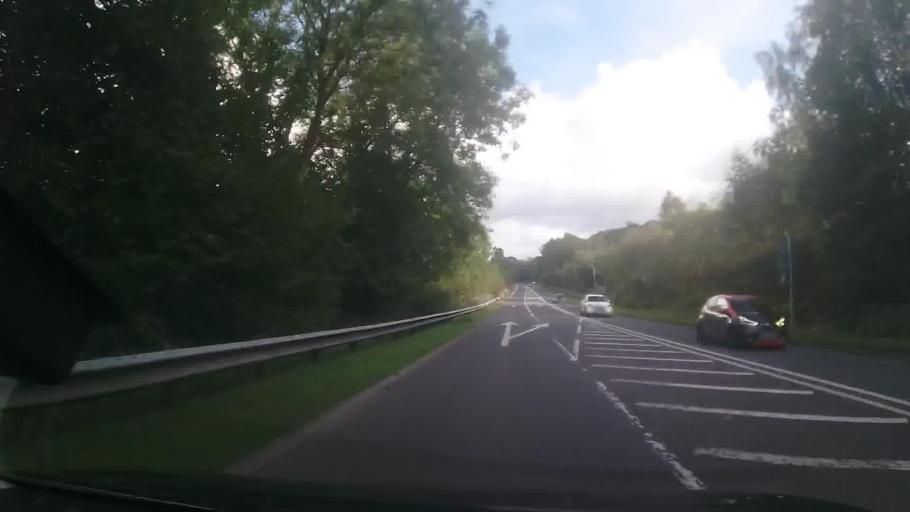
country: GB
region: Wales
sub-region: Gwynedd
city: Dolgellau
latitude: 52.7496
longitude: -3.8470
